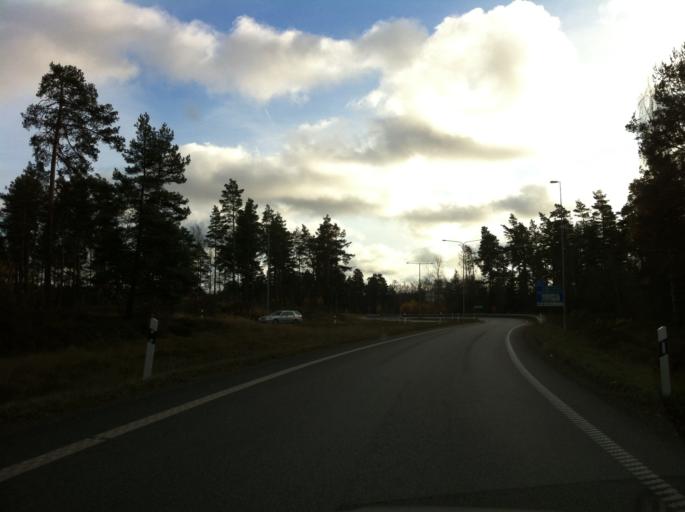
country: SE
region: Kronoberg
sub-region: Vaxjo Kommun
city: Gemla
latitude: 56.8428
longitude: 14.7118
